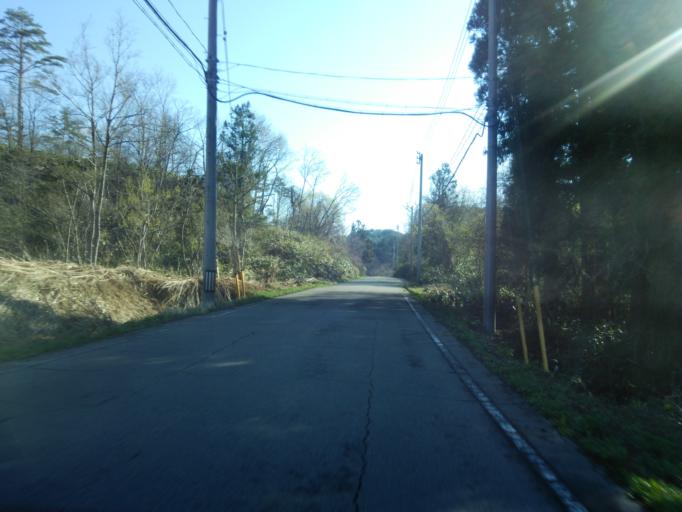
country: JP
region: Fukushima
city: Kitakata
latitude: 37.6493
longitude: 139.7948
